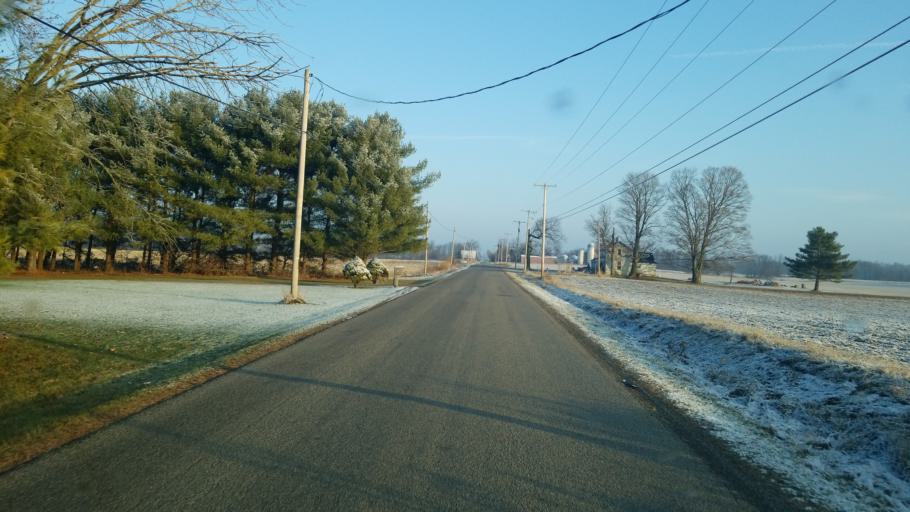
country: US
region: Ohio
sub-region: Morrow County
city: Mount Gilead
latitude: 40.6242
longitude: -82.8603
